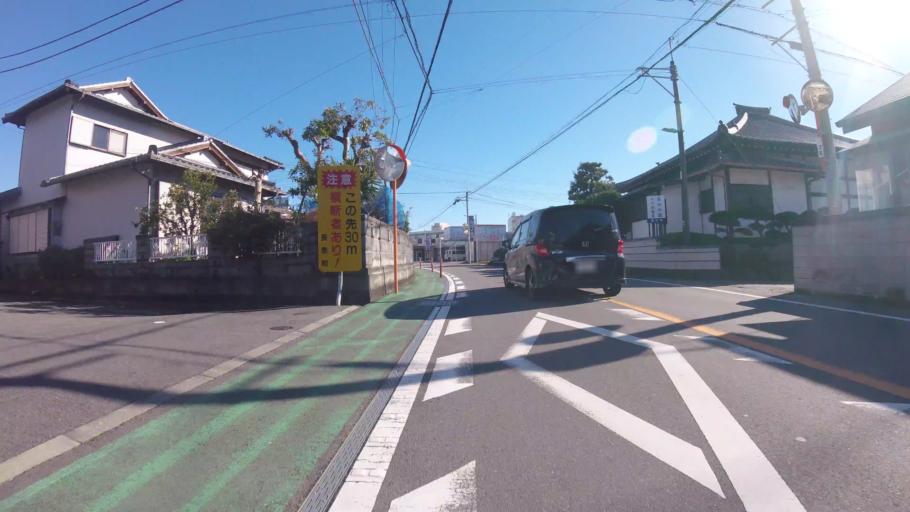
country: JP
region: Shizuoka
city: Mishima
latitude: 35.1202
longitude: 138.8889
